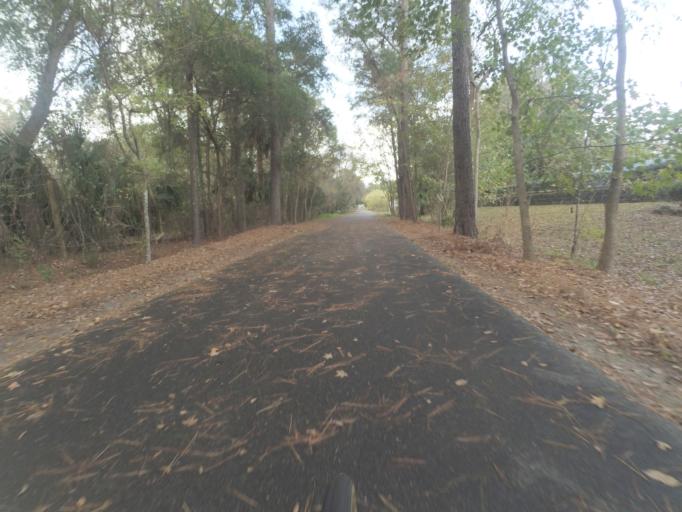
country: US
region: Florida
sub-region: Alachua County
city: Gainesville
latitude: 29.6391
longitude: -82.3189
